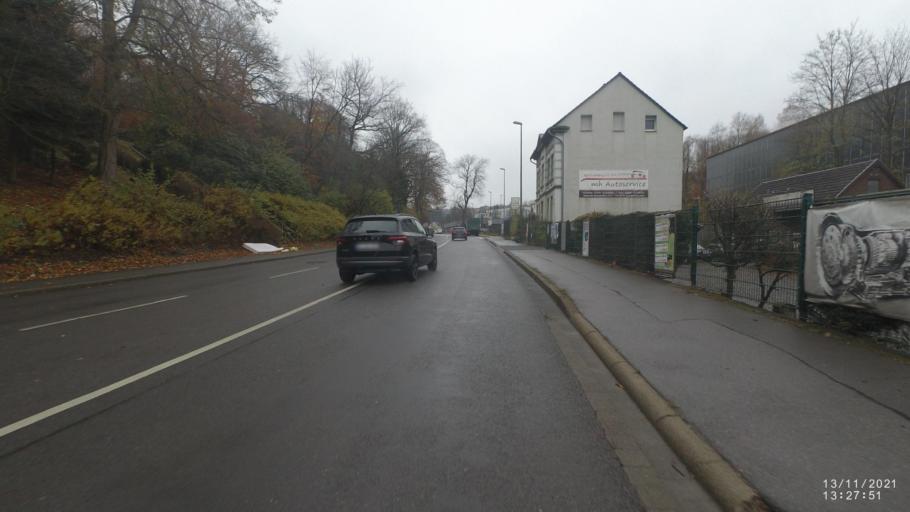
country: DE
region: North Rhine-Westphalia
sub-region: Regierungsbezirk Arnsberg
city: Luedenscheid
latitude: 51.2315
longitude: 7.6328
